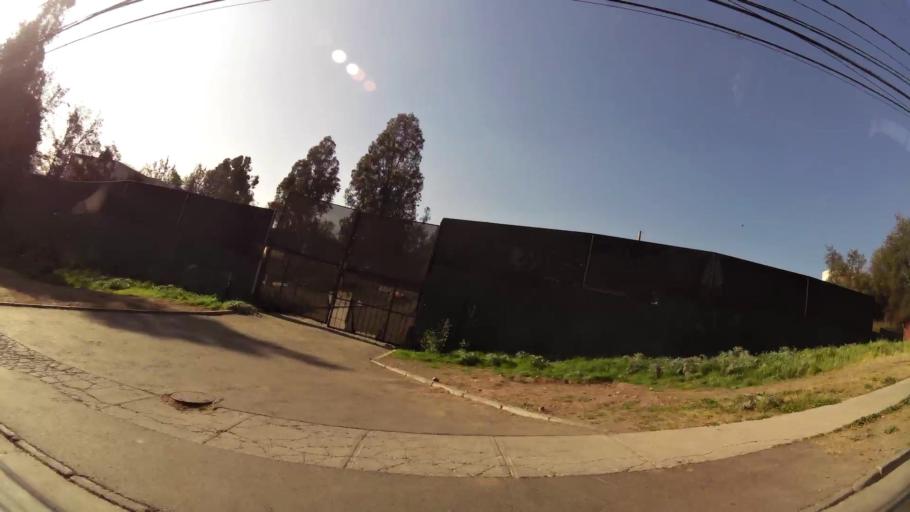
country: CL
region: Santiago Metropolitan
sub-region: Provincia de Santiago
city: Villa Presidente Frei, Nunoa, Santiago, Chile
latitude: -33.3516
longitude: -70.5041
